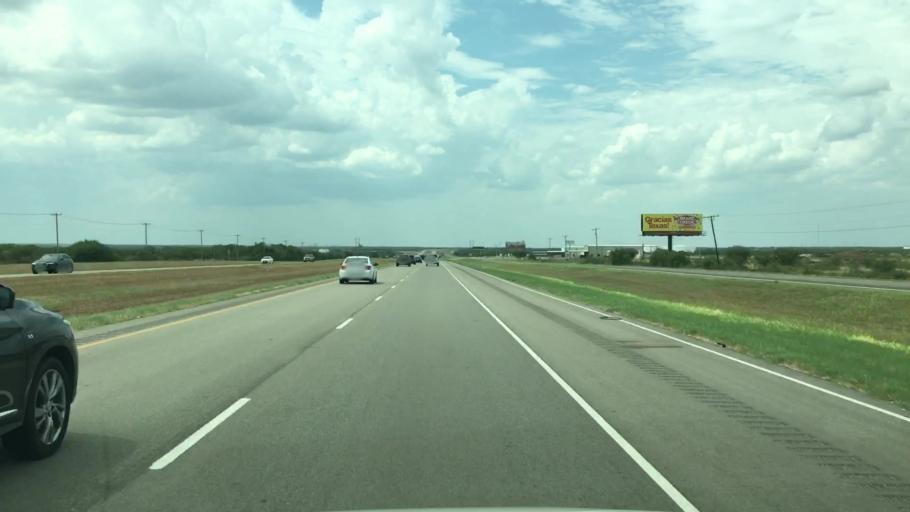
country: US
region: Texas
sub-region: Live Oak County
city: Three Rivers
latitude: 28.5063
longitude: -98.1629
